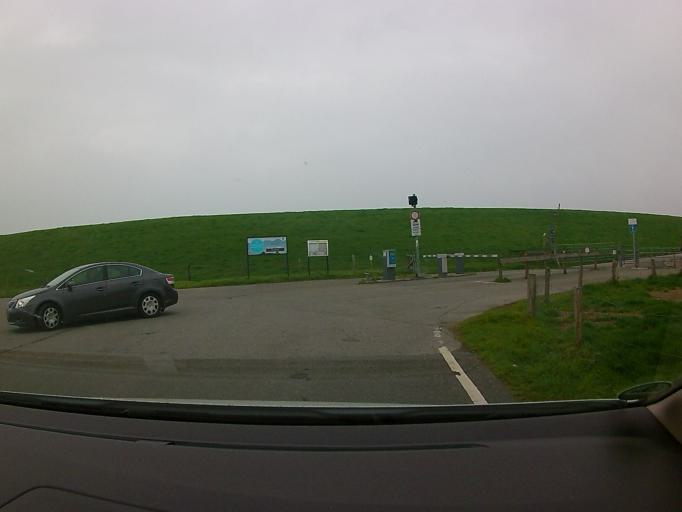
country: DE
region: Schleswig-Holstein
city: Reussenkoge
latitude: 54.6157
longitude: 8.8701
